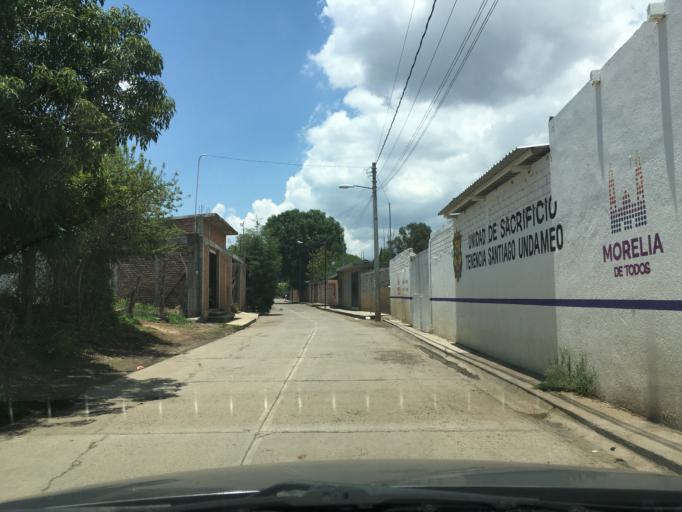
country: MX
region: Michoacan
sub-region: Morelia
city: La Mintzita (Piedra Dura)
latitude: 19.5941
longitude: -101.2833
